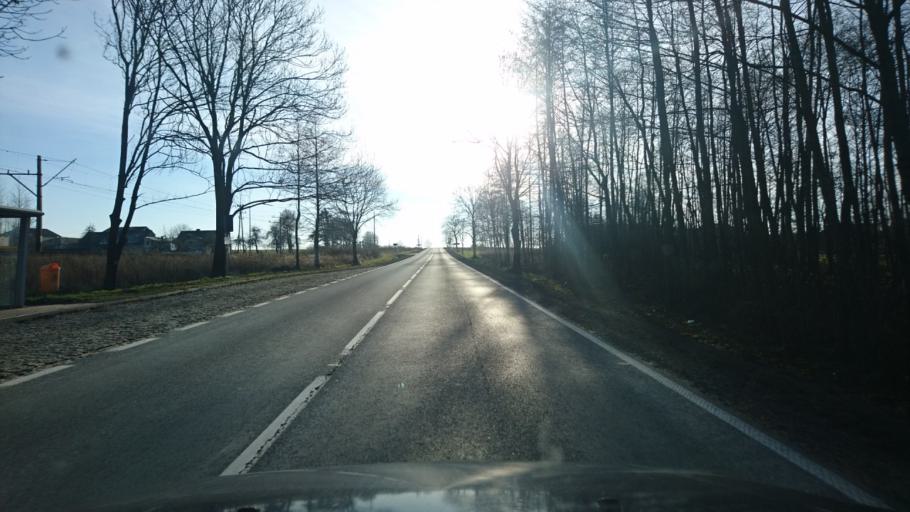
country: PL
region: Opole Voivodeship
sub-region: Powiat oleski
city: Dalachow
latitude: 51.0659
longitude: 18.6008
